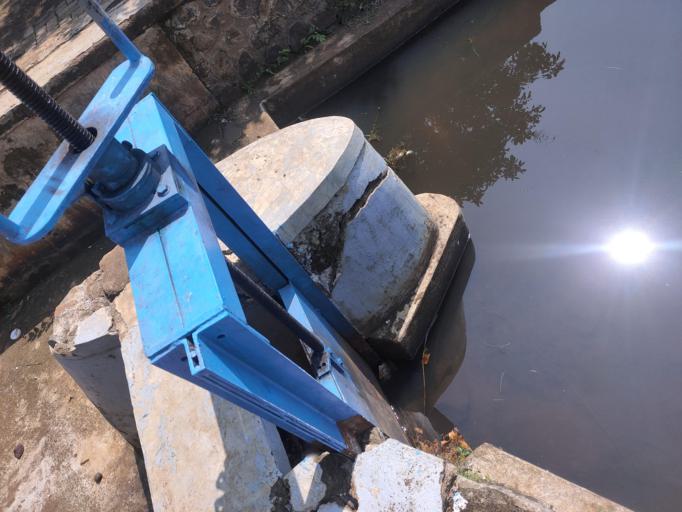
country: ID
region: West Java
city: Ciampea
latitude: -6.4808
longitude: 106.6609
